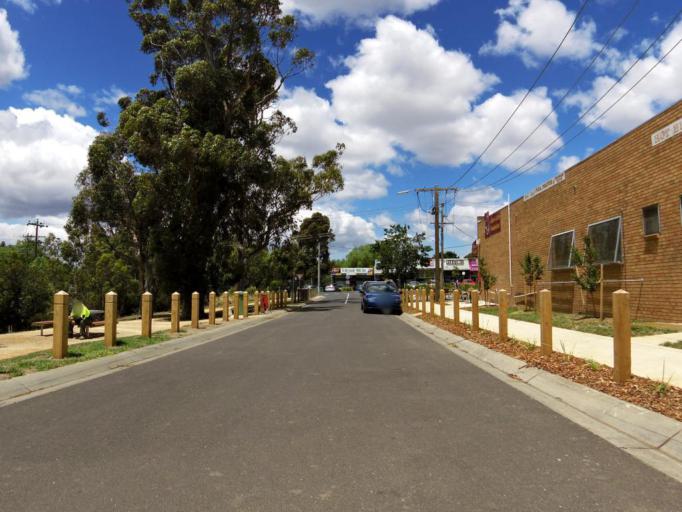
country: AU
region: Victoria
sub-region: Hume
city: Westmeadows
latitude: -37.6760
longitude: 144.8869
